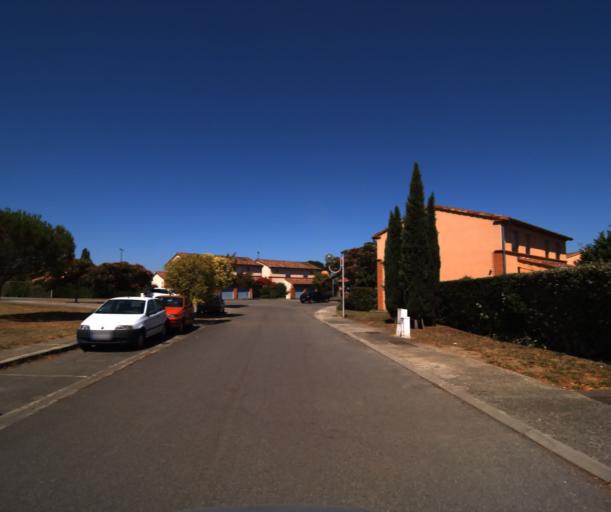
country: FR
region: Midi-Pyrenees
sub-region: Departement de la Haute-Garonne
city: Muret
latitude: 43.4711
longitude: 1.3250
